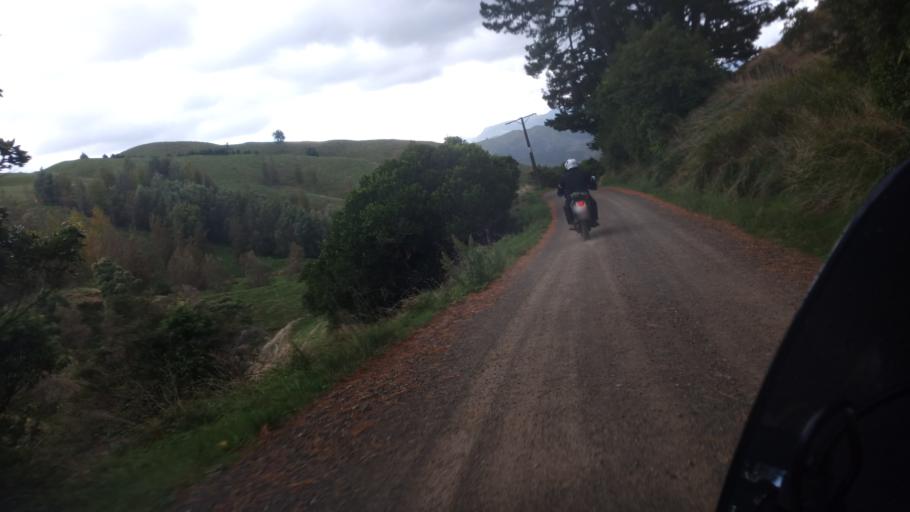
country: NZ
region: Gisborne
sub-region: Gisborne District
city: Gisborne
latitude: -38.4797
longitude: 177.6102
